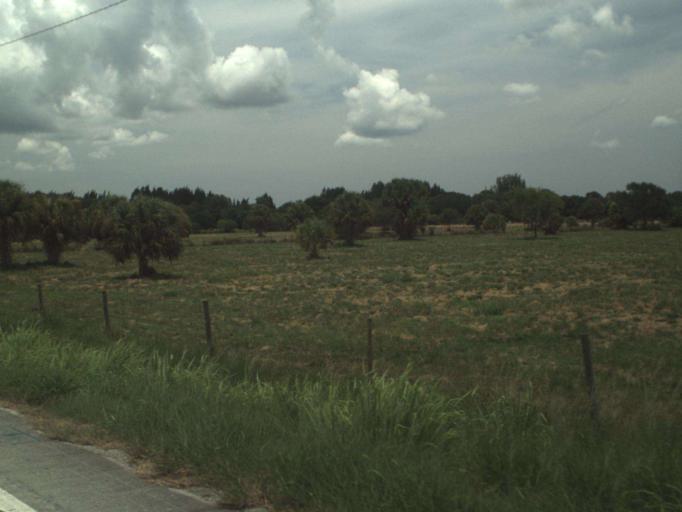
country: US
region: Florida
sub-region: Saint Lucie County
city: Fort Pierce South
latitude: 27.4265
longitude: -80.3991
